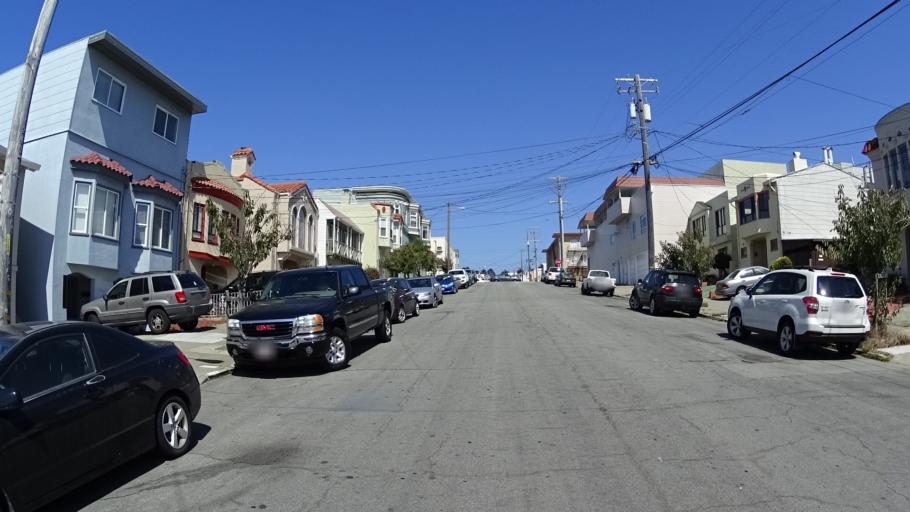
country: US
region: California
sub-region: San Mateo County
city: Daly City
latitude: 37.7419
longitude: -122.4842
